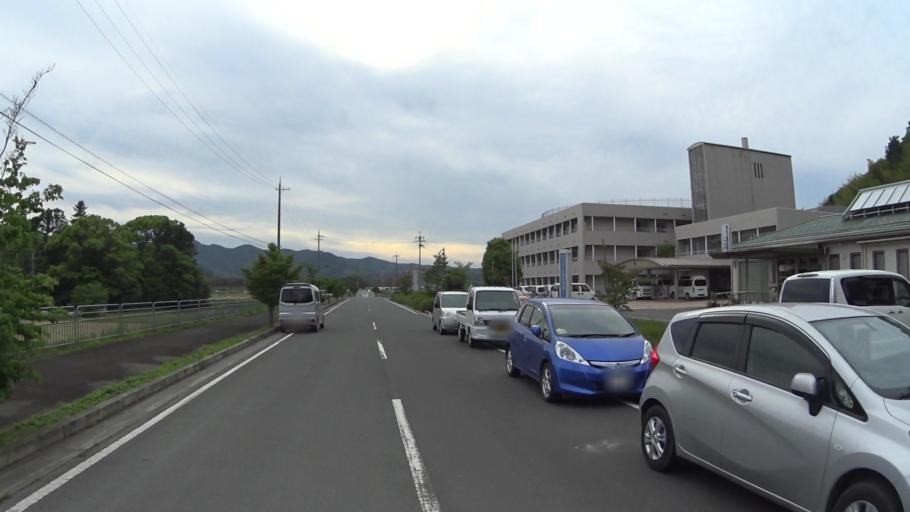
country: JP
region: Kyoto
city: Kameoka
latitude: 35.0772
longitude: 135.5411
